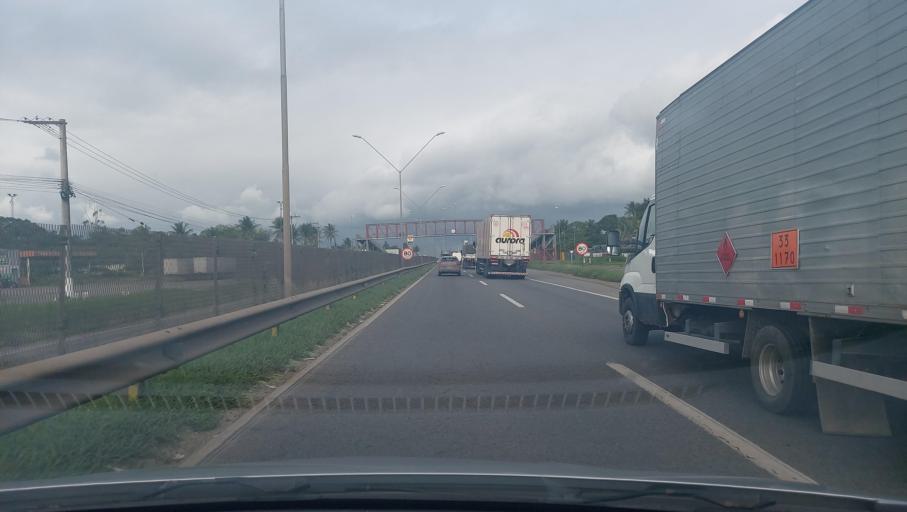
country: BR
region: Bahia
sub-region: Feira De Santana
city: Feira de Santana
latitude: -12.3128
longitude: -38.8820
